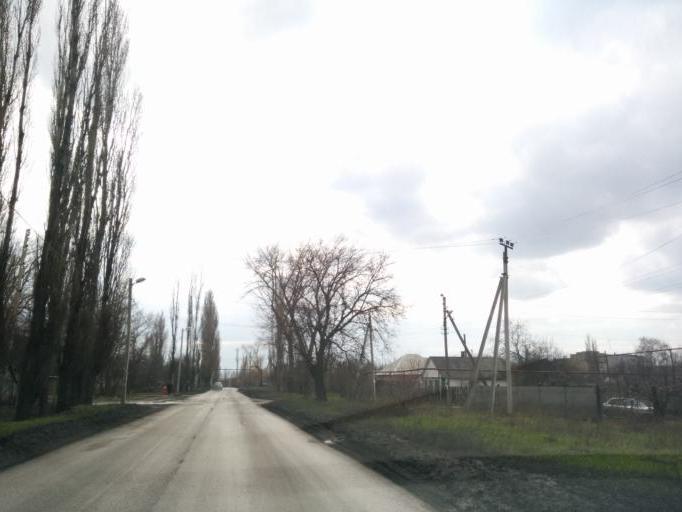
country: RU
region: Rostov
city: Shakhty
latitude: 47.6857
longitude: 40.2872
